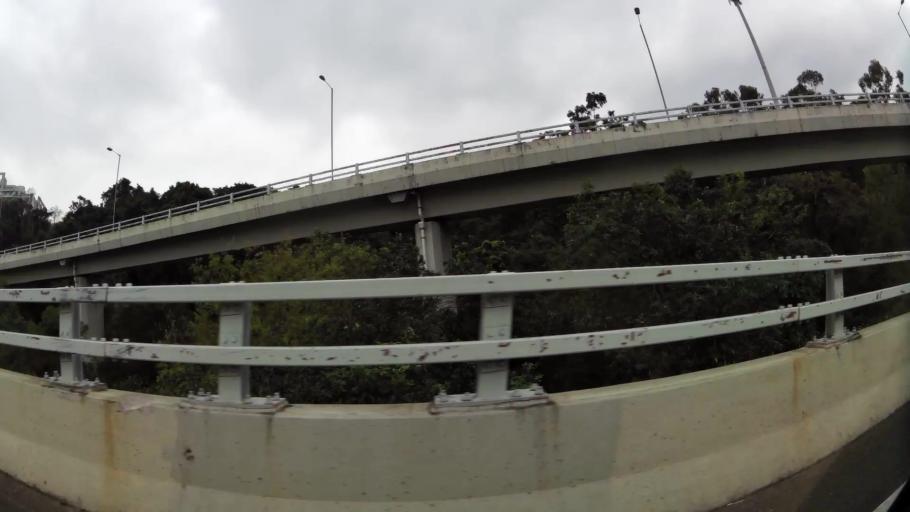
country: HK
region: Sha Tin
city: Sha Tin
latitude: 22.3784
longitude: 114.1791
